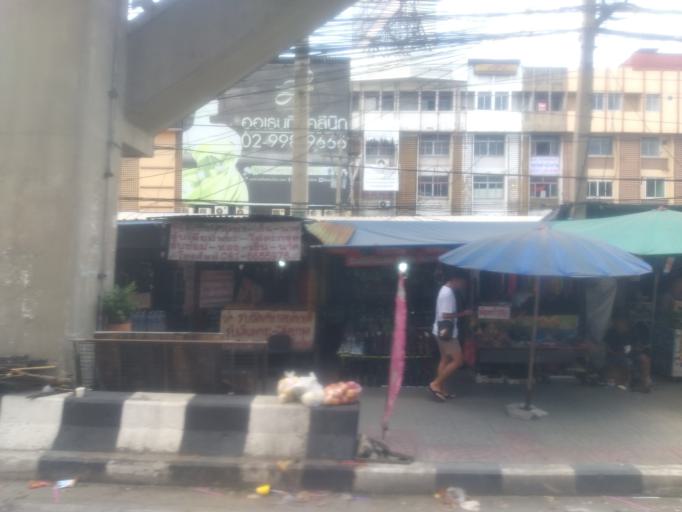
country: TH
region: Bangkok
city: Sai Mai
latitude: 13.9617
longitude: 100.6205
